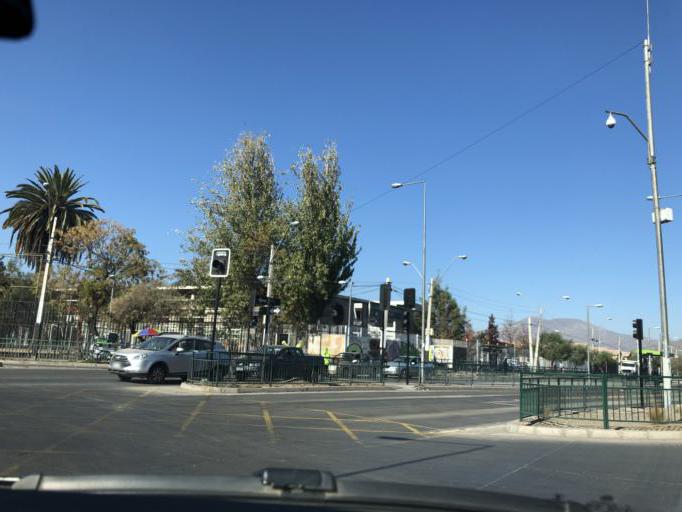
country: CL
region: Santiago Metropolitan
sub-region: Provincia de Santiago
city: La Pintana
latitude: -33.6185
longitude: -70.6265
